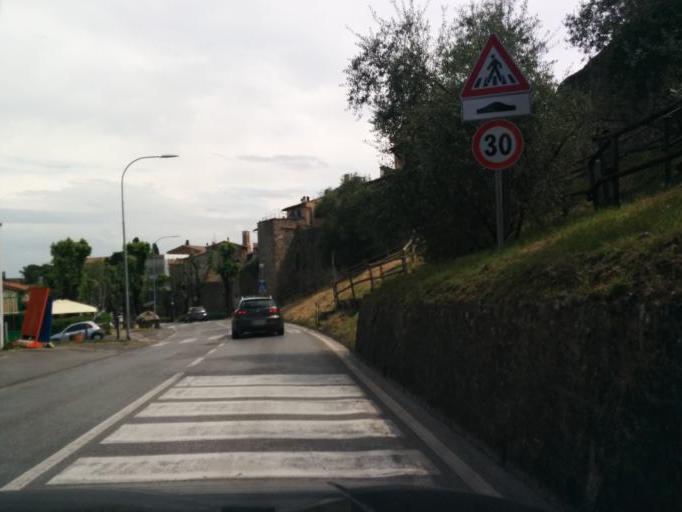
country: IT
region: Tuscany
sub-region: Provincia di Siena
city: San Gimignano
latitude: 43.4687
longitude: 11.0403
